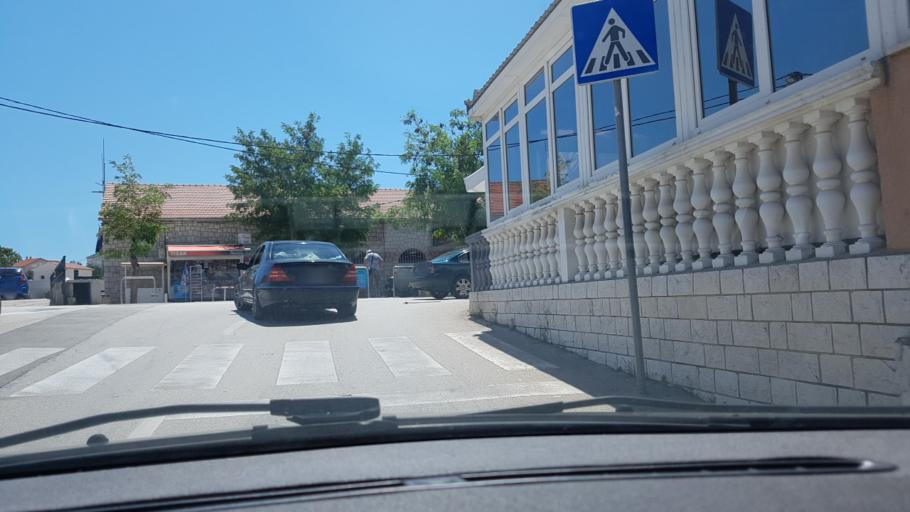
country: HR
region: Splitsko-Dalmatinska
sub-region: Grad Trogir
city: Trogir
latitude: 43.4937
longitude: 16.2640
